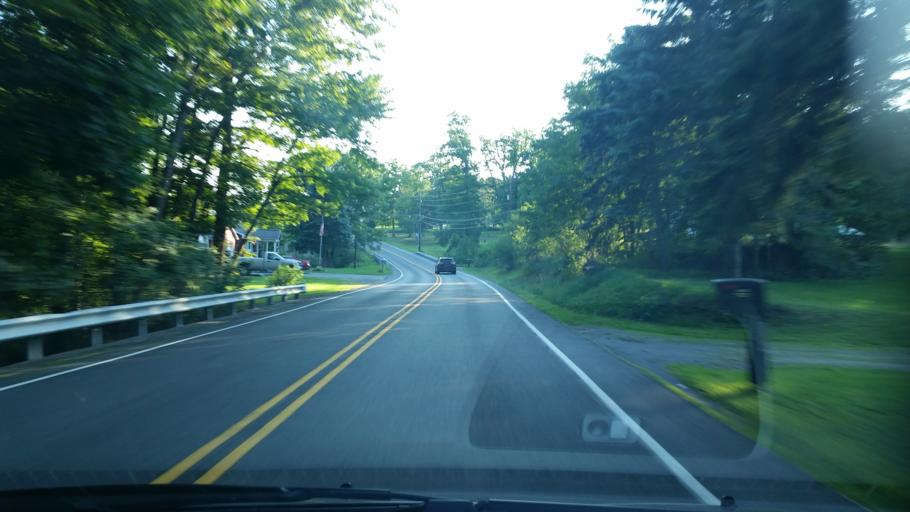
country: US
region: Pennsylvania
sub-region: Blair County
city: Greenwood
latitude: 40.5669
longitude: -78.3794
